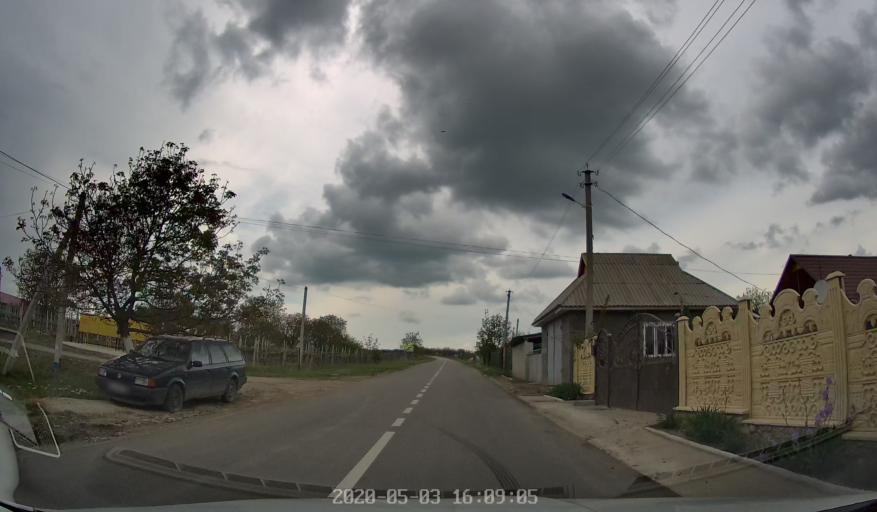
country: MD
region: Calarasi
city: Calarasi
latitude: 47.1990
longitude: 28.3405
